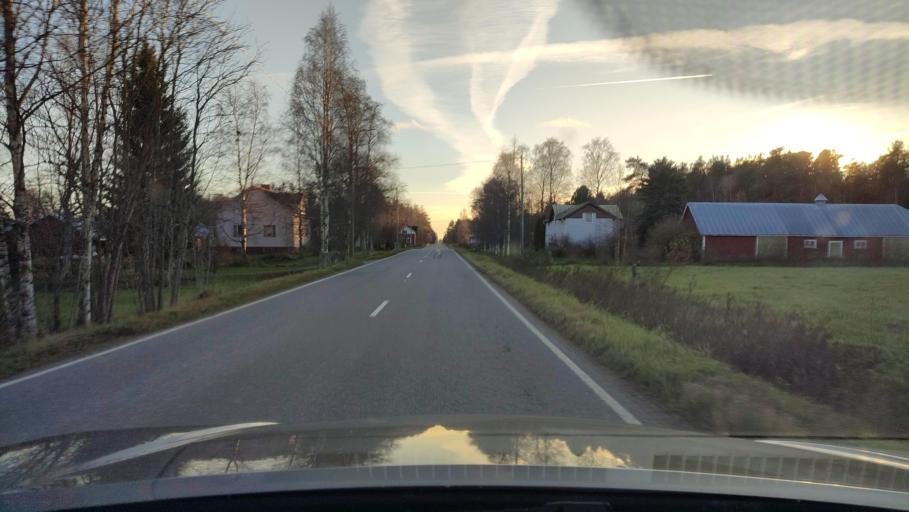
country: FI
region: Ostrobothnia
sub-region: Sydosterbotten
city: Naerpes
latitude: 62.6487
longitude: 21.5105
